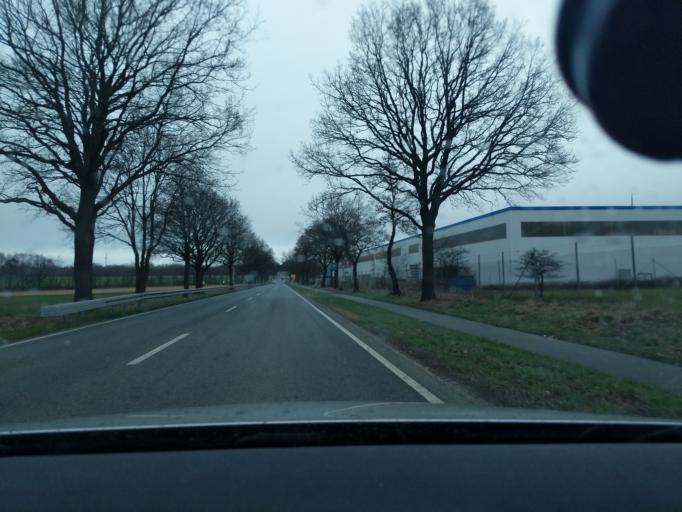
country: DE
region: Lower Saxony
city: Hammah
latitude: 53.5787
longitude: 9.4025
